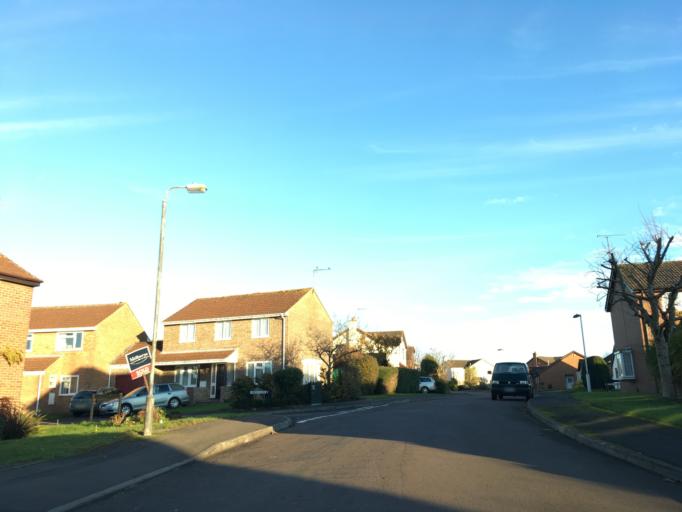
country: GB
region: England
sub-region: South Gloucestershire
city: Thornbury
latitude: 51.6159
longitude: -2.5146
